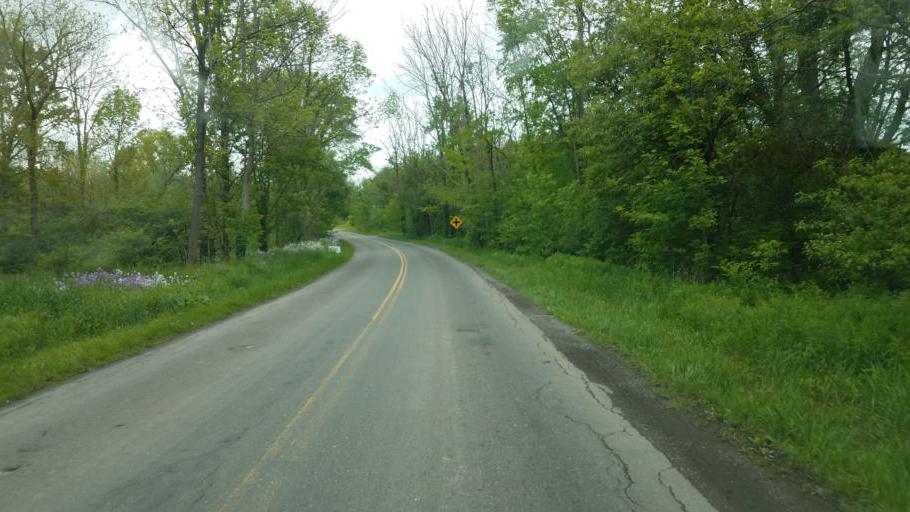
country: US
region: Ohio
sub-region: Geauga County
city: Middlefield
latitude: 41.4405
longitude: -80.9729
